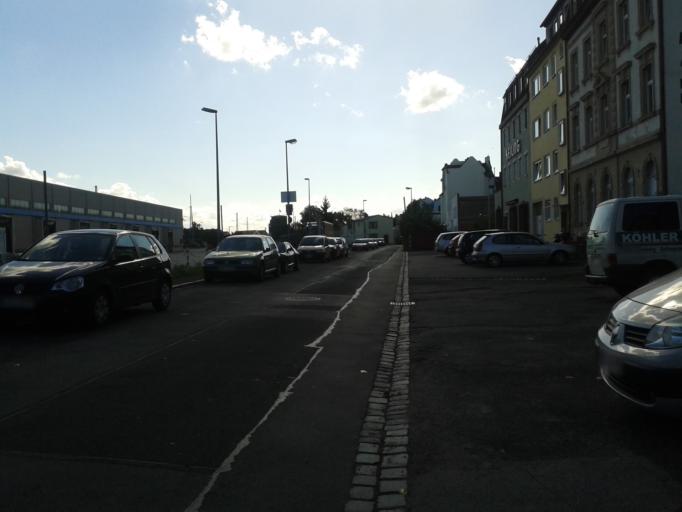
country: DE
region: Bavaria
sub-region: Upper Franconia
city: Bamberg
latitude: 49.8959
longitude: 10.9040
